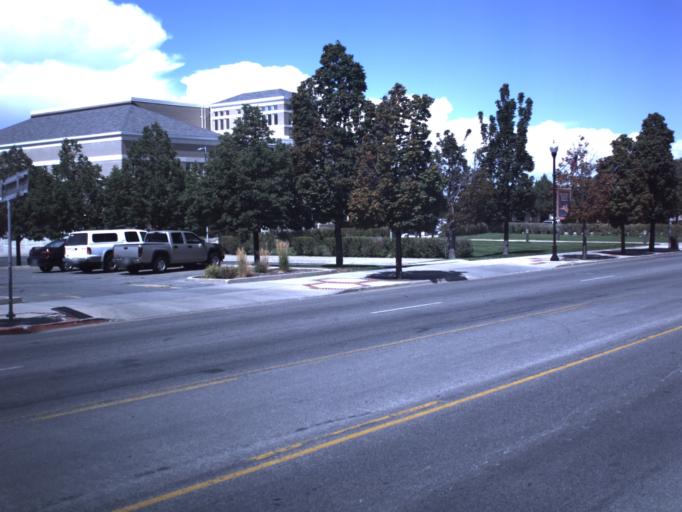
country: US
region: Utah
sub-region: Box Elder County
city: Brigham City
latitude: 41.5109
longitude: -112.0157
